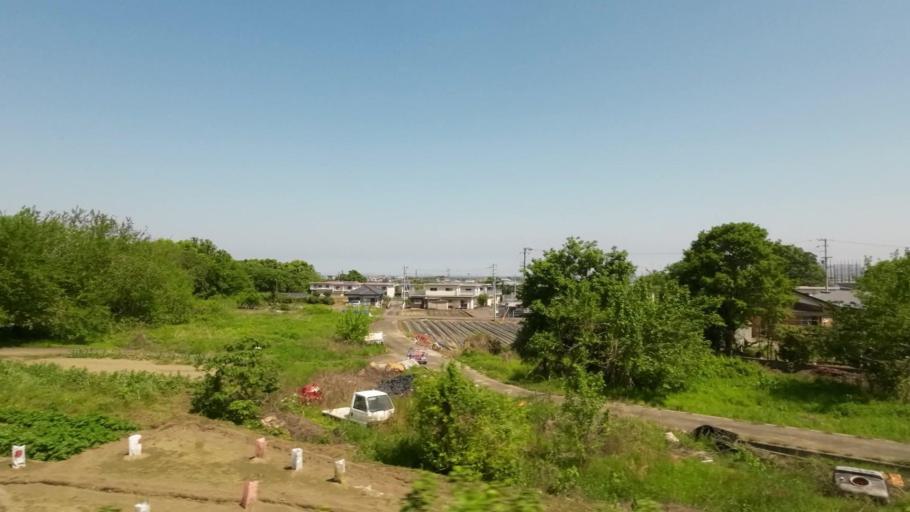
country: JP
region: Ehime
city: Kawanoecho
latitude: 33.9640
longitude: 133.4475
